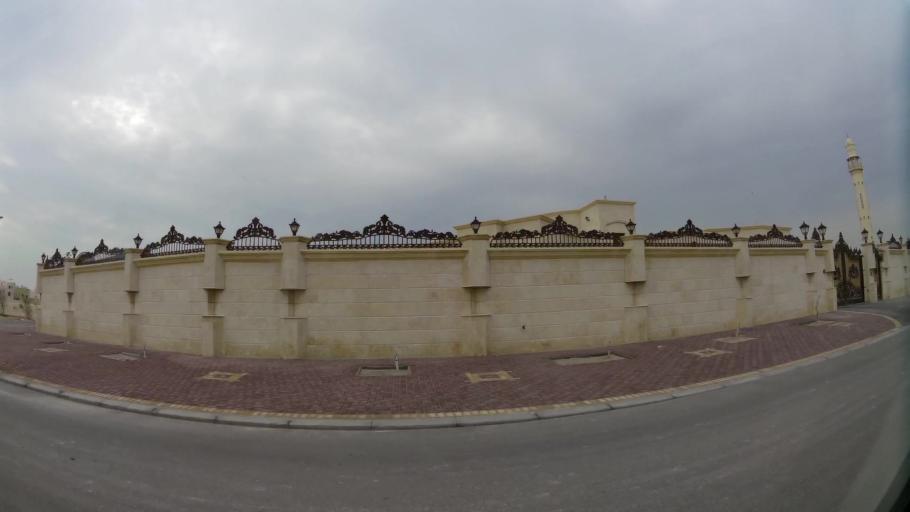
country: BH
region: Northern
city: Ar Rifa'
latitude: 26.0540
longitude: 50.6199
